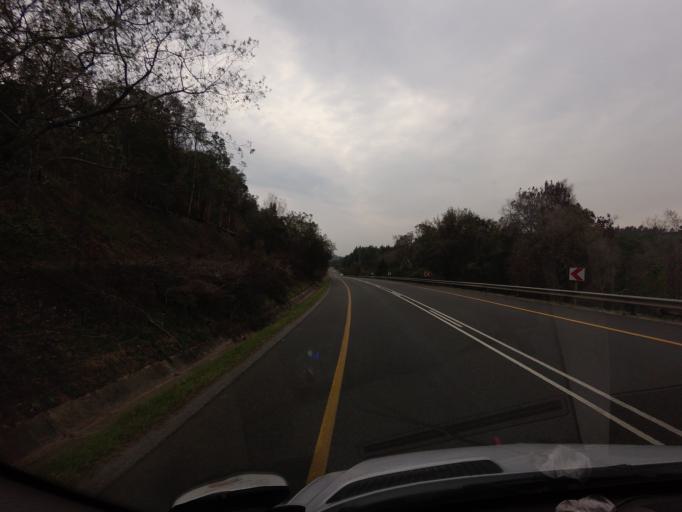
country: ZA
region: Western Cape
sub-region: Eden District Municipality
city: Knysna
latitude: -34.0343
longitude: 23.1583
